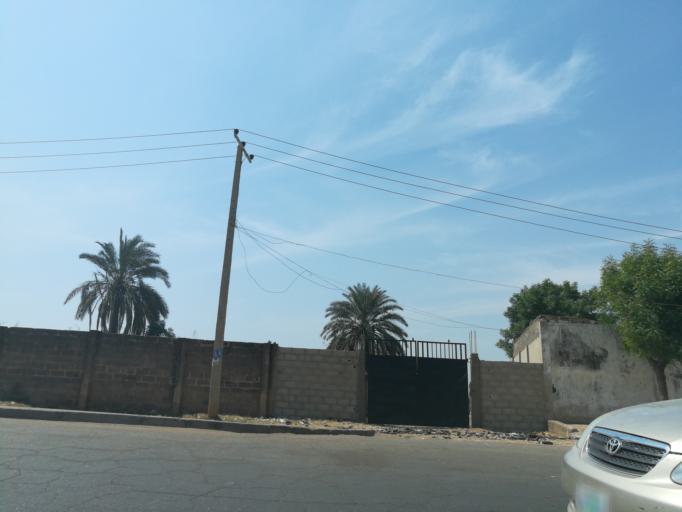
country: NG
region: Kano
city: Kano
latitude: 12.0221
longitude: 8.5167
